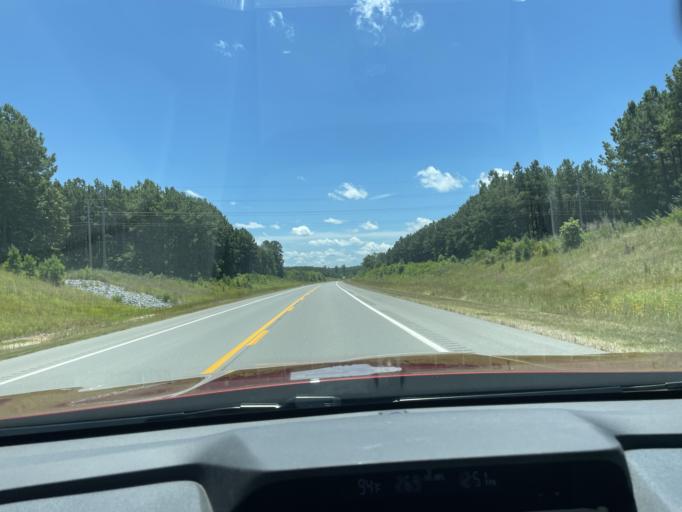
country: US
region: Arkansas
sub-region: Lincoln County
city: Star City
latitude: 33.9300
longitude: -91.8883
